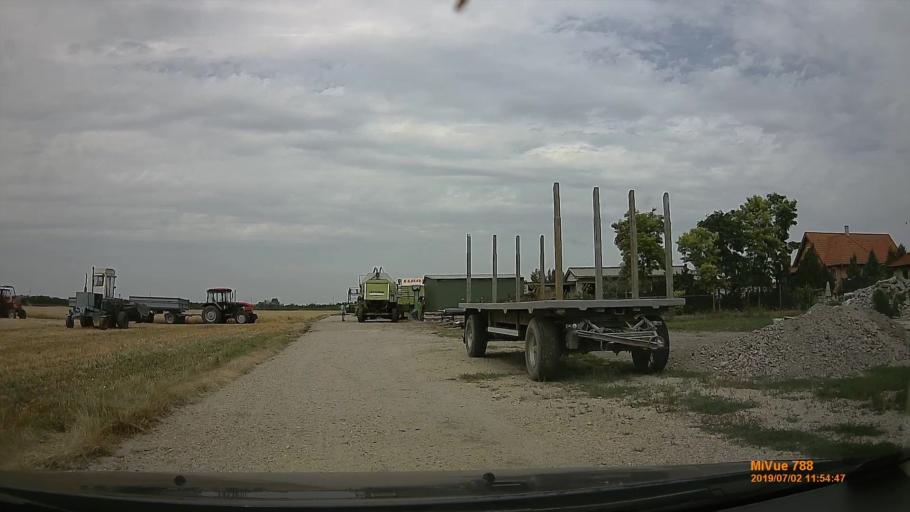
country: HU
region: Gyor-Moson-Sopron
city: Janossomorja
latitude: 47.8457
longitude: 17.1698
